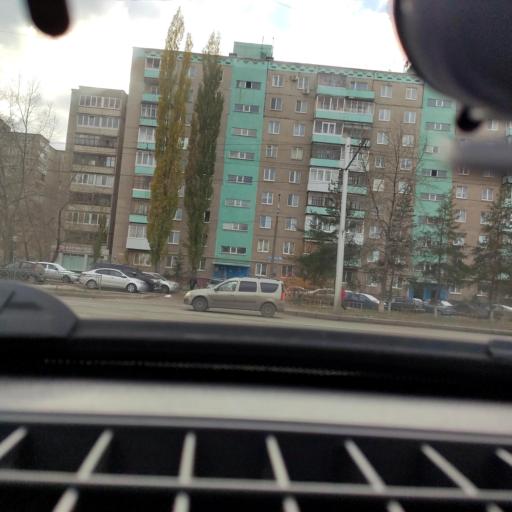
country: RU
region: Bashkortostan
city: Ufa
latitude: 54.7707
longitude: 56.0557
